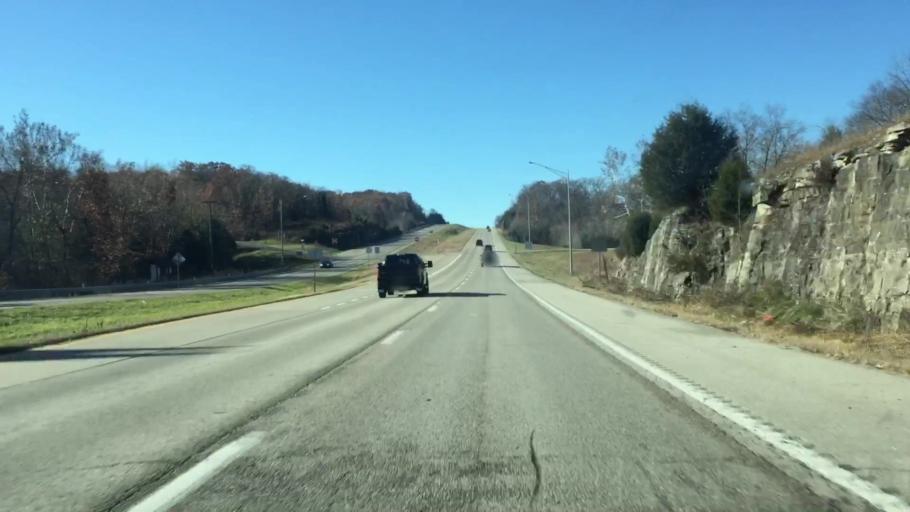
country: US
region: Missouri
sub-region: Cole County
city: Wardsville
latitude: 38.5189
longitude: -92.2340
